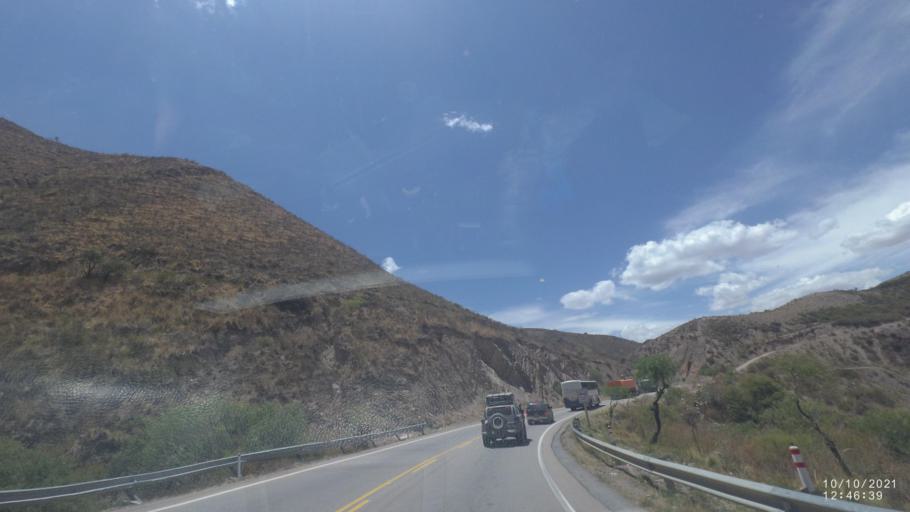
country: BO
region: Cochabamba
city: Irpa Irpa
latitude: -17.6327
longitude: -66.3652
